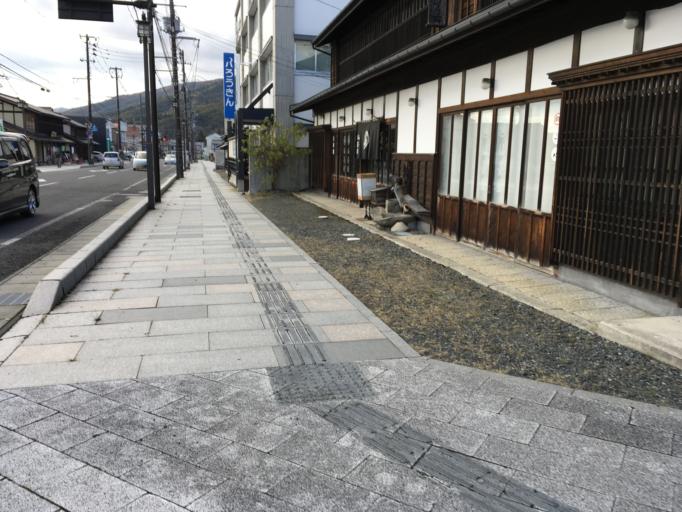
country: JP
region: Iwate
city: Tono
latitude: 39.3297
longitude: 141.5295
